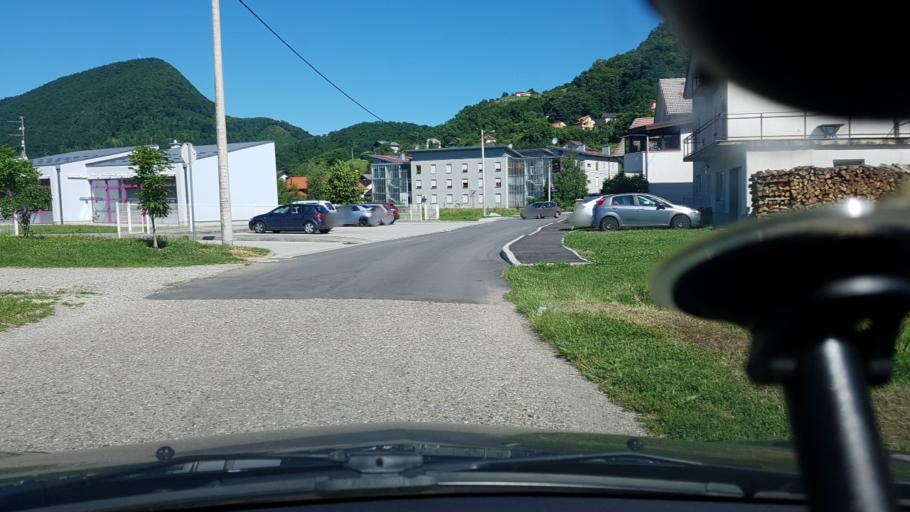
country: HR
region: Krapinsko-Zagorska
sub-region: Grad Krapina
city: Krapina
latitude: 46.1792
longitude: 15.8651
